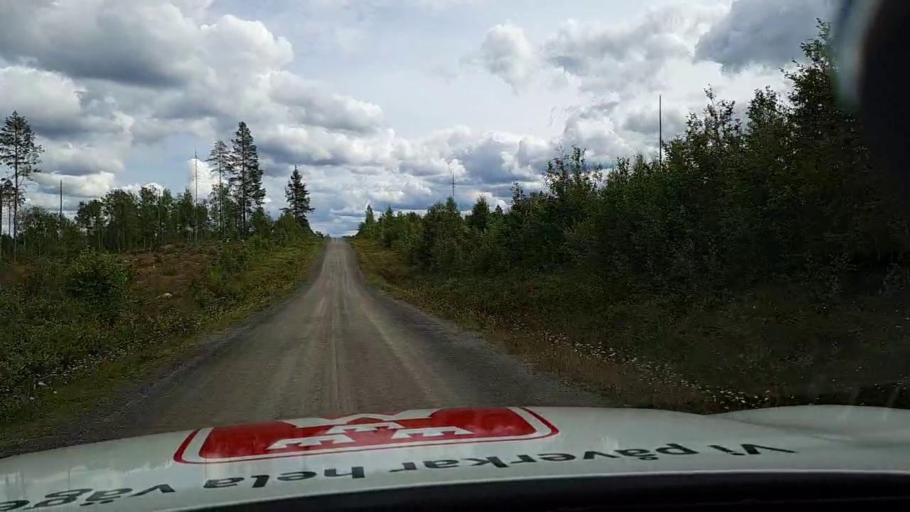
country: SE
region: Jaemtland
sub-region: OEstersunds Kommun
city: Lit
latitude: 63.2954
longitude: 15.3347
